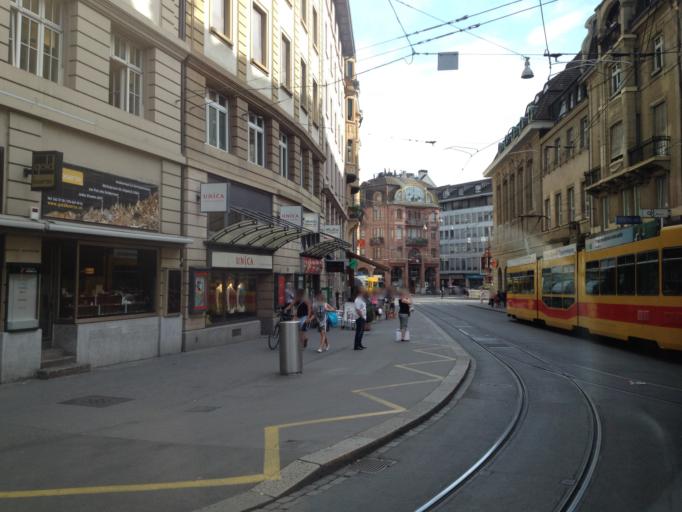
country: CH
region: Basel-City
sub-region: Basel-Stadt
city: Basel
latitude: 47.5598
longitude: 7.5879
